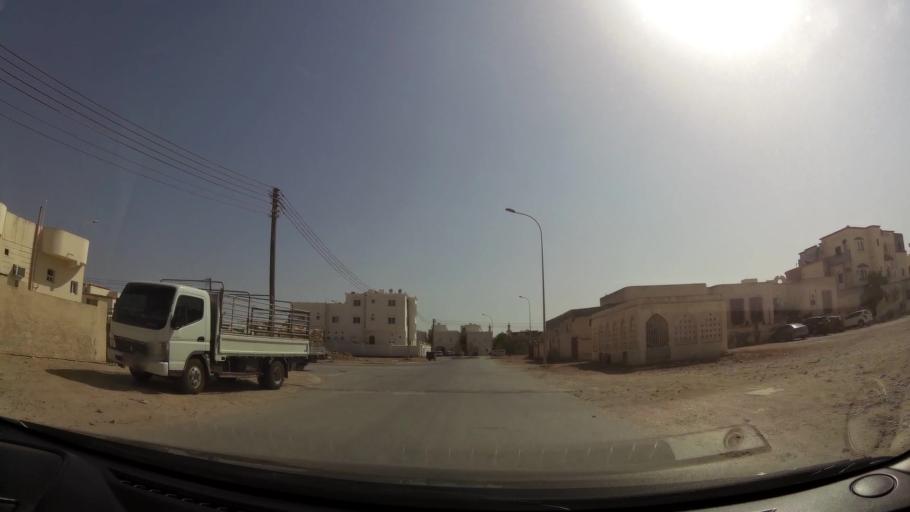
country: OM
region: Zufar
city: Salalah
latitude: 17.0031
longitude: 54.0177
